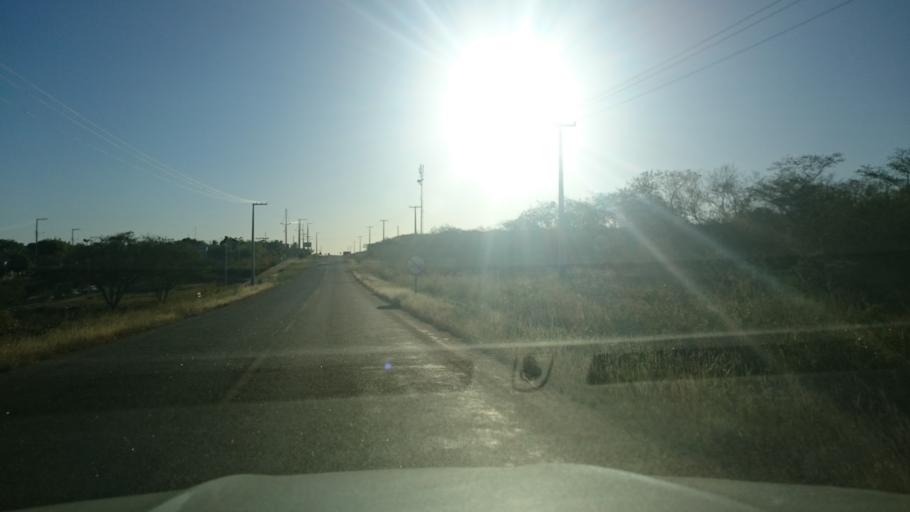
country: BR
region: Rio Grande do Norte
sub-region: Umarizal
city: Umarizal
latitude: -5.9336
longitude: -37.9308
